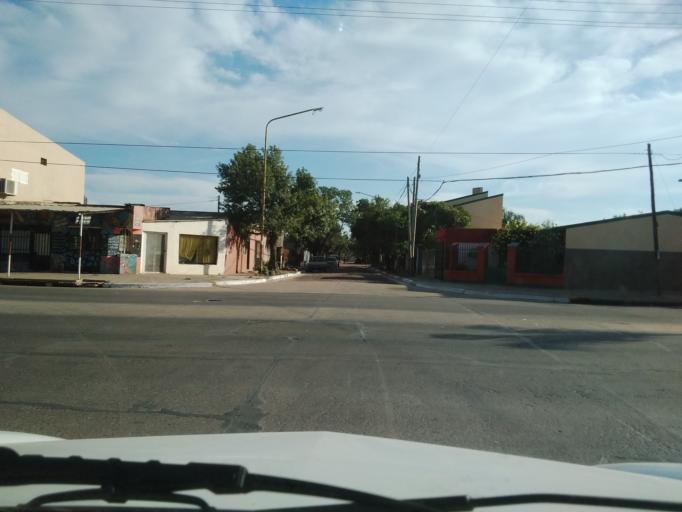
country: AR
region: Corrientes
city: Corrientes
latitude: -27.4903
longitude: -58.7839
